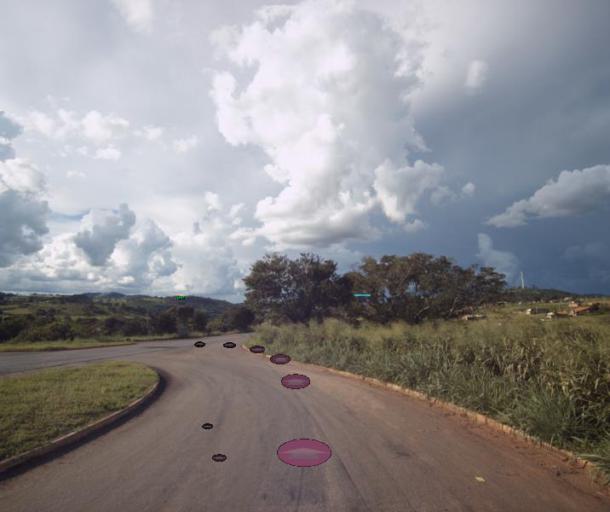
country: BR
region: Goias
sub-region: Rialma
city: Rialma
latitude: -15.3102
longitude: -49.5719
